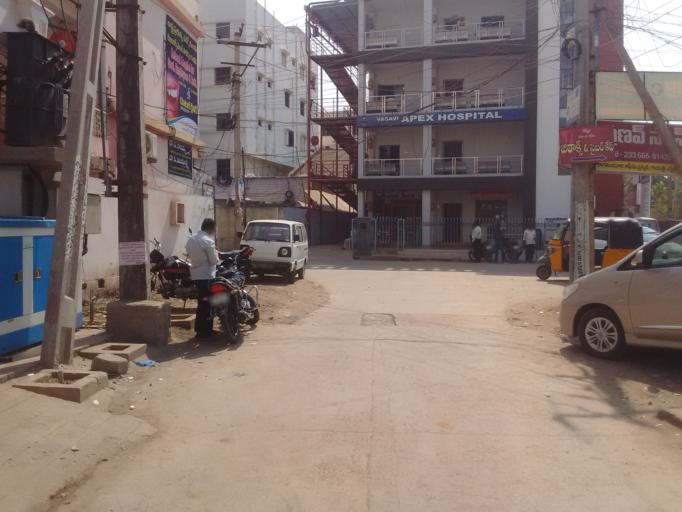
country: IN
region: Telangana
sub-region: Mahbubnagar
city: Alampur
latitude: 15.8126
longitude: 78.0397
